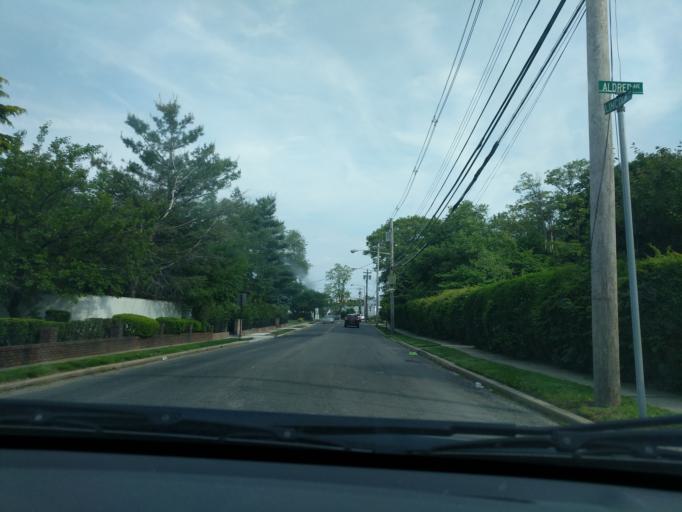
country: US
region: New York
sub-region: Nassau County
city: Oceanside
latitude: 40.6485
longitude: -73.6392
